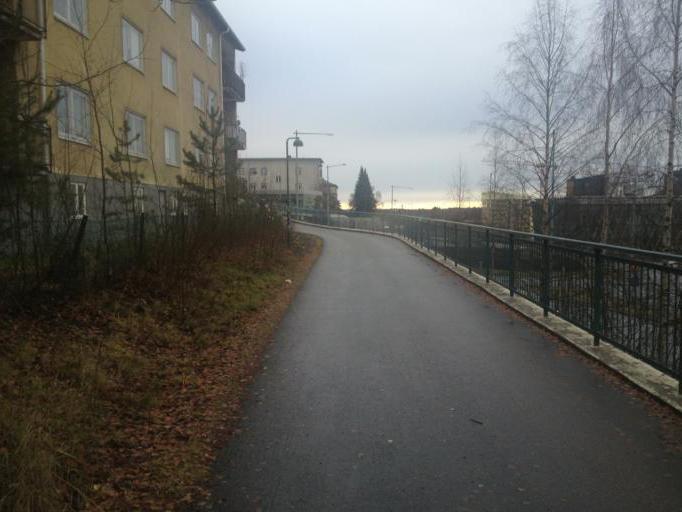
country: SE
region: Vaesterbotten
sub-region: Umea Kommun
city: Umea
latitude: 63.8187
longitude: 20.2950
